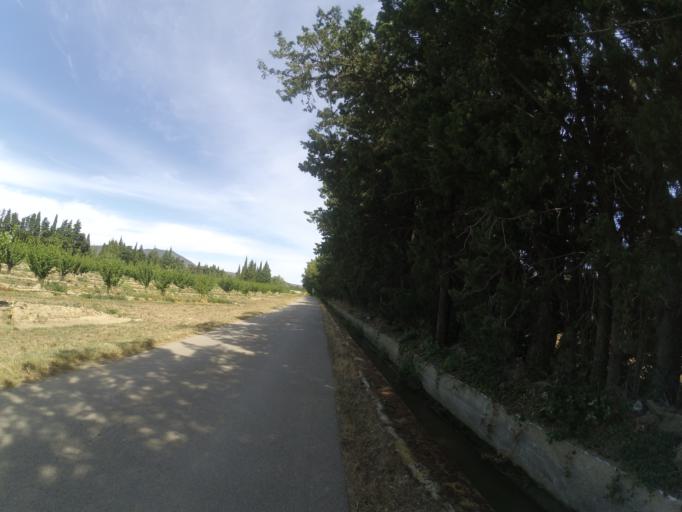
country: FR
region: Languedoc-Roussillon
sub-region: Departement des Pyrenees-Orientales
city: Millas
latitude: 42.6857
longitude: 2.6793
